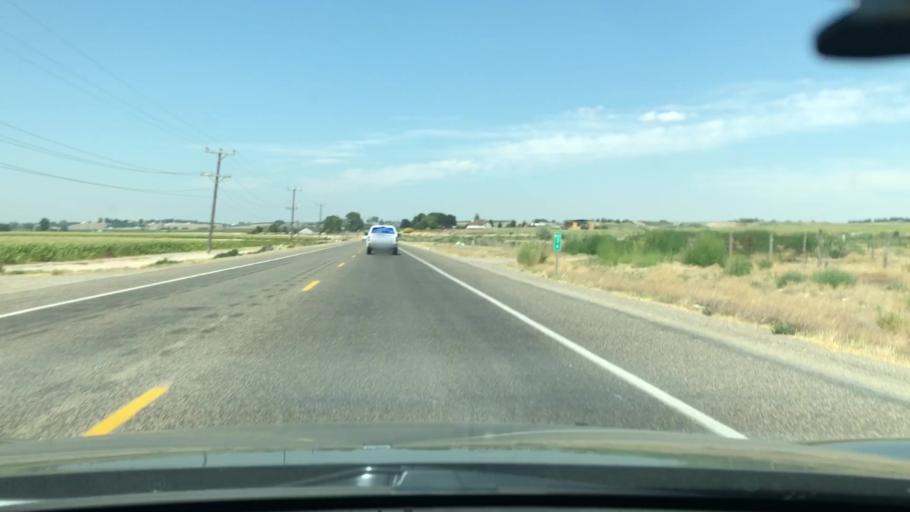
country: US
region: Idaho
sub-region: Owyhee County
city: Homedale
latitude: 43.6335
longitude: -116.9116
